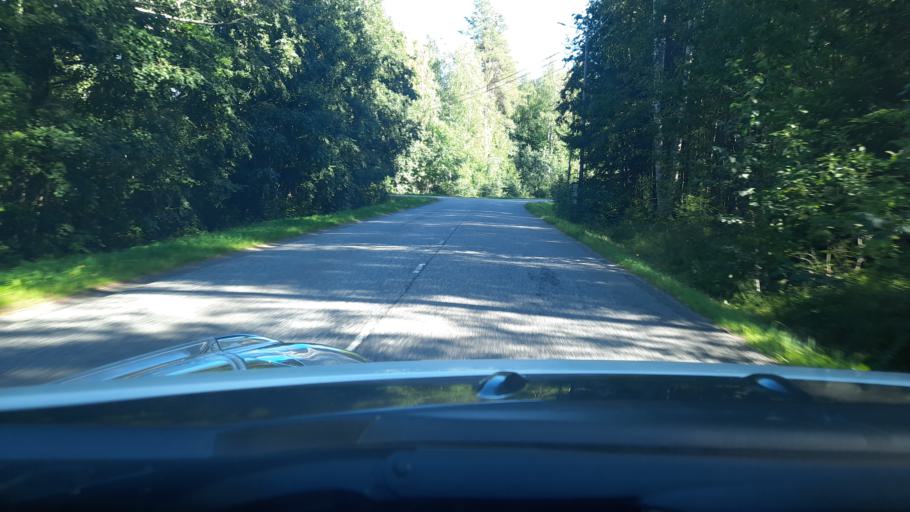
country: FI
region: North Karelia
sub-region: Joensuu
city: Joensuu
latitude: 62.6355
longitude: 29.6982
